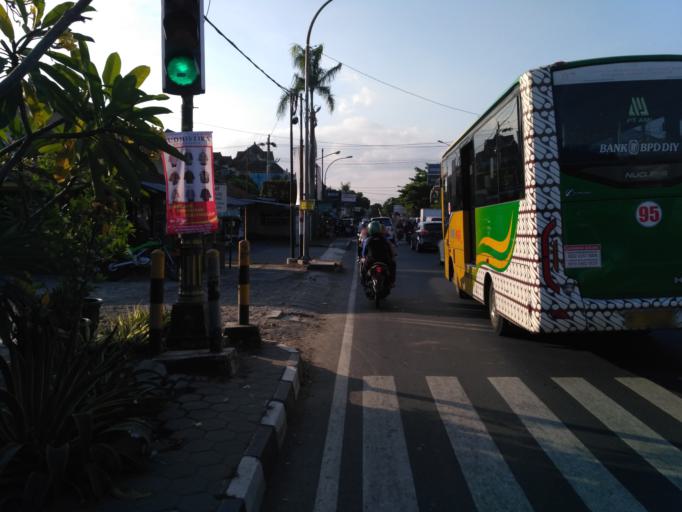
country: ID
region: Daerah Istimewa Yogyakarta
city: Sewon
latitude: -7.8323
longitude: 110.3901
